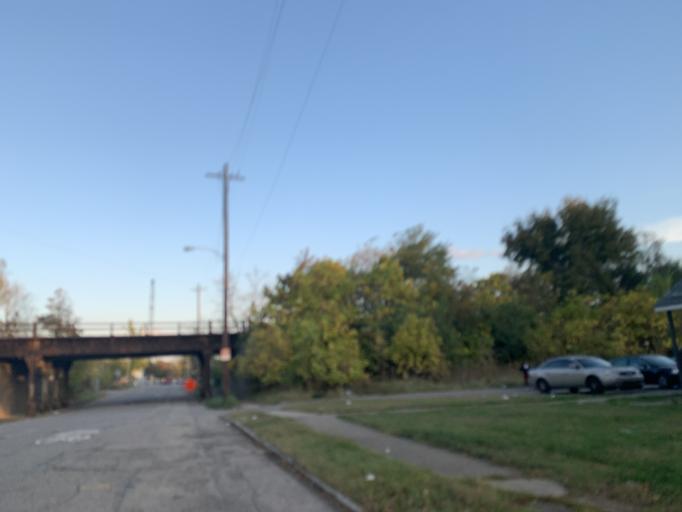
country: US
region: Indiana
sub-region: Floyd County
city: New Albany
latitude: 38.2551
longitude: -85.8038
